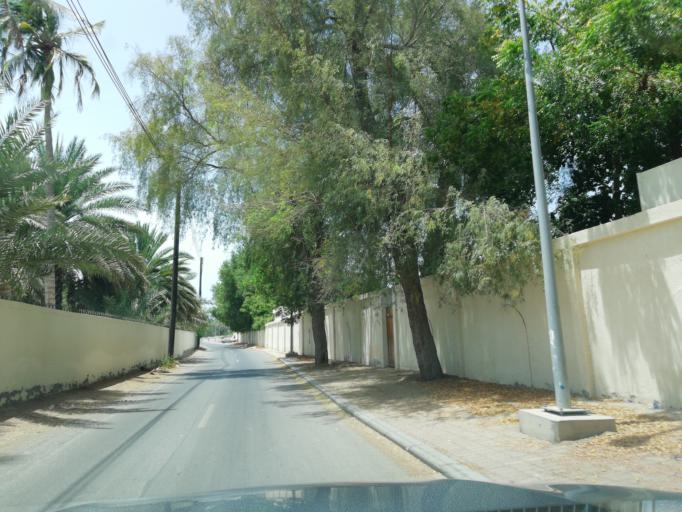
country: OM
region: Muhafazat Masqat
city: As Sib al Jadidah
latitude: 23.6623
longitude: 58.2069
